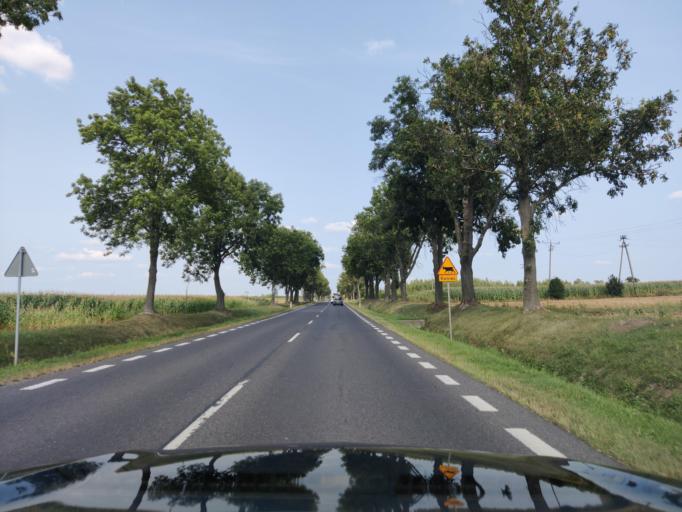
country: PL
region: Masovian Voivodeship
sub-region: Powiat pultuski
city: Pultusk
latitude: 52.7465
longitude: 21.1000
